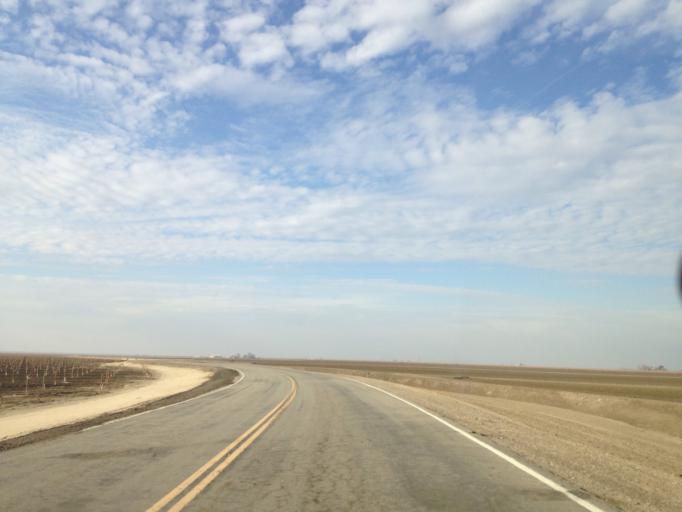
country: US
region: California
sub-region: Kern County
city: Buttonwillow
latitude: 35.4423
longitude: -119.5506
